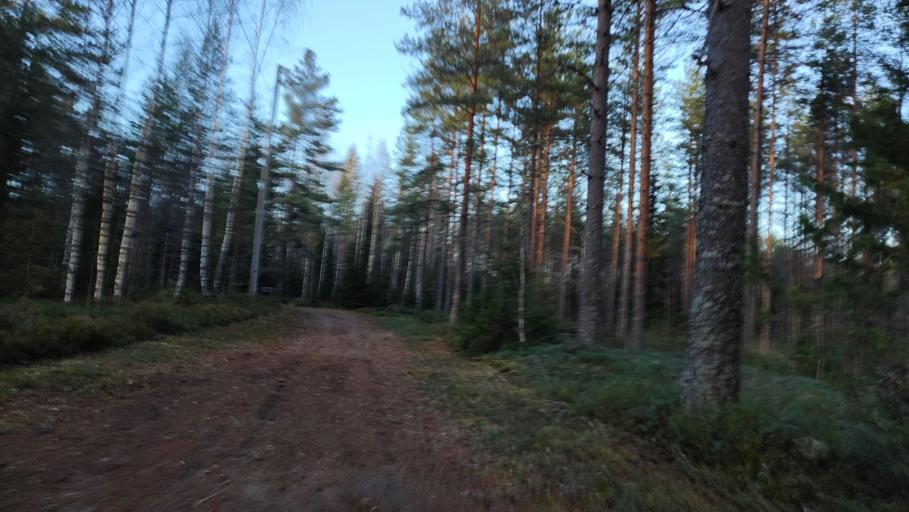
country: FI
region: Southern Ostrobothnia
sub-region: Suupohja
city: Karijoki
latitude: 62.2782
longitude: 21.6298
